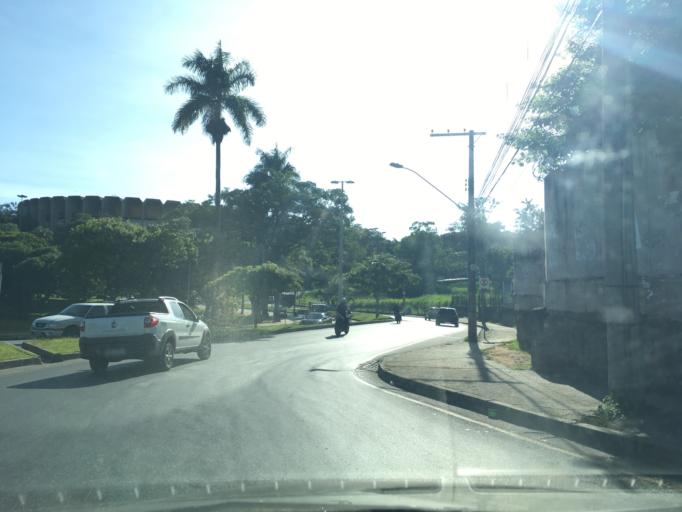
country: BR
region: Minas Gerais
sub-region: Belo Horizonte
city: Belo Horizonte
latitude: -19.8630
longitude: -43.9760
